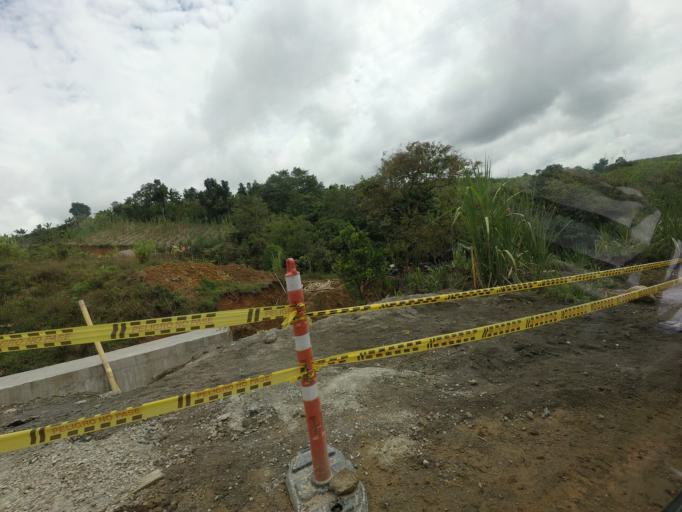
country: CO
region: Huila
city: San Agustin
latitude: 1.9569
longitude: -76.2958
